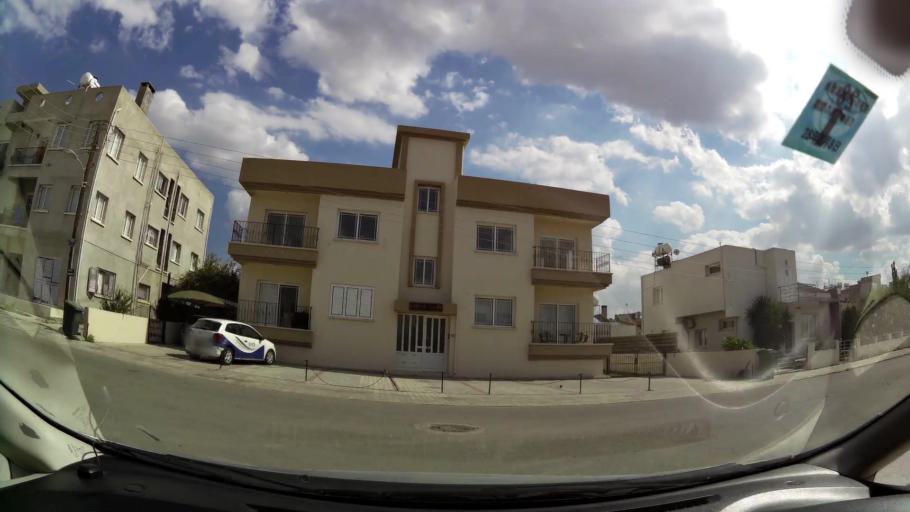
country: CY
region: Lefkosia
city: Nicosia
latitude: 35.2164
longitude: 33.3004
